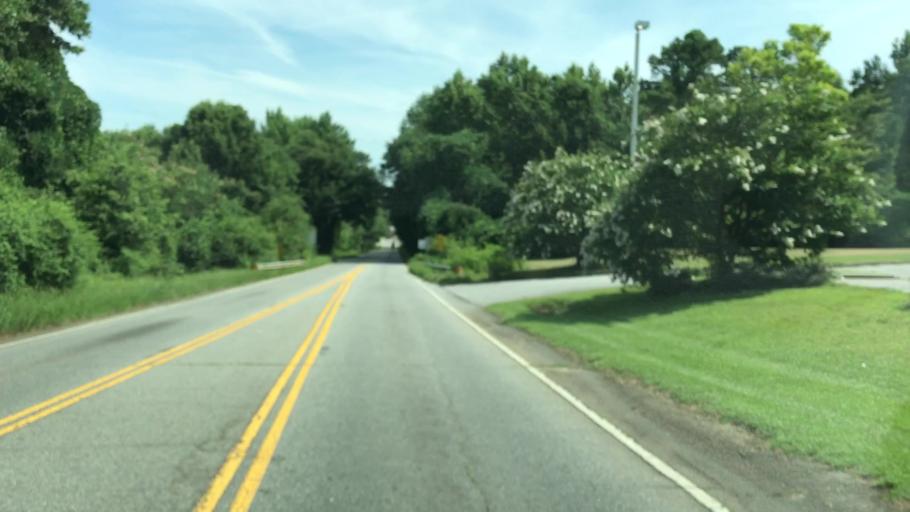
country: US
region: South Carolina
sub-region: Anderson County
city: Williamston
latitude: 34.6327
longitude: -82.4683
